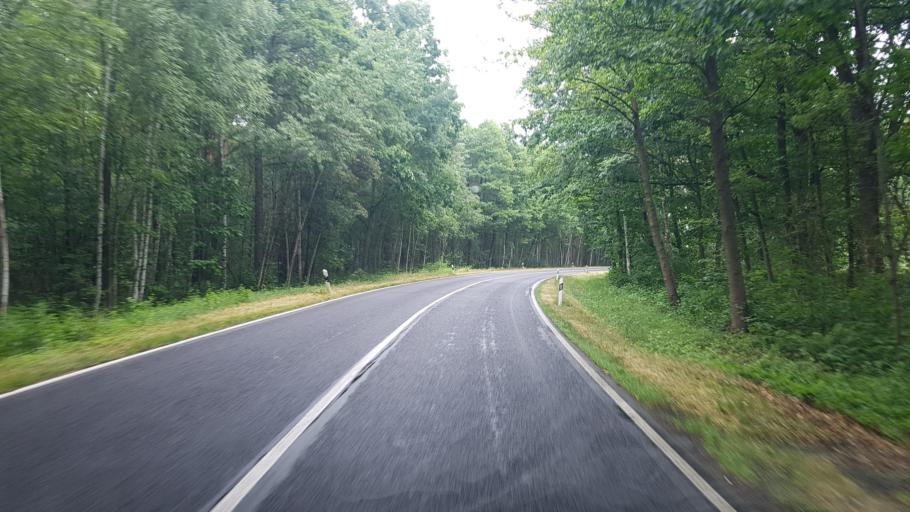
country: DE
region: Brandenburg
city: Kroppen
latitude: 51.3890
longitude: 13.8203
